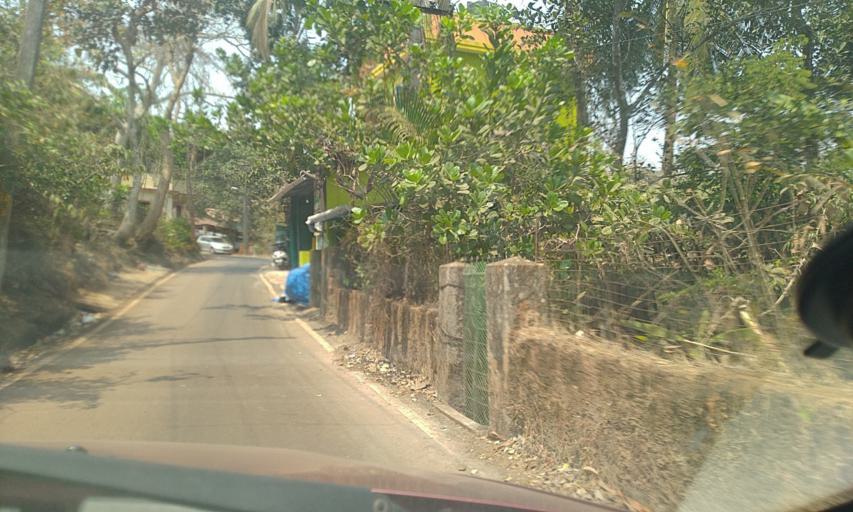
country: IN
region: Goa
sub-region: North Goa
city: Serula
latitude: 15.5225
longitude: 73.8403
